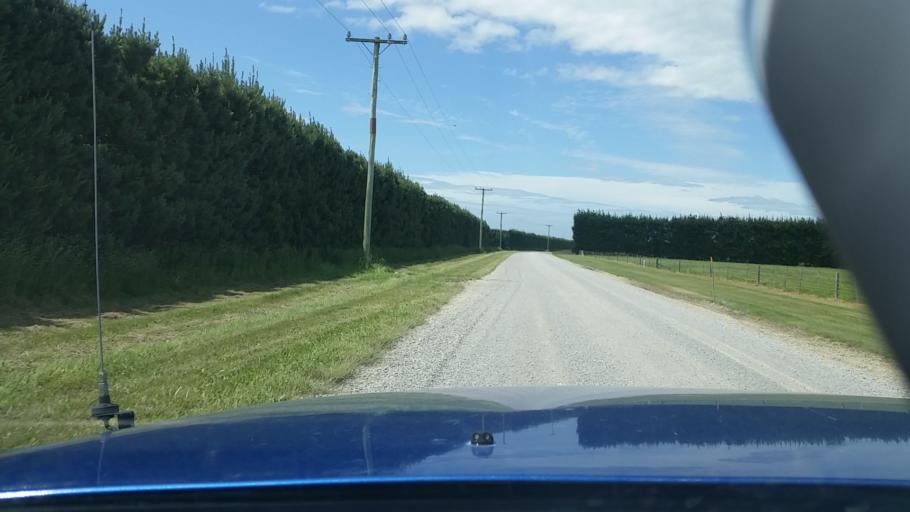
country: NZ
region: Canterbury
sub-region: Ashburton District
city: Ashburton
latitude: -43.9739
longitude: 171.9330
